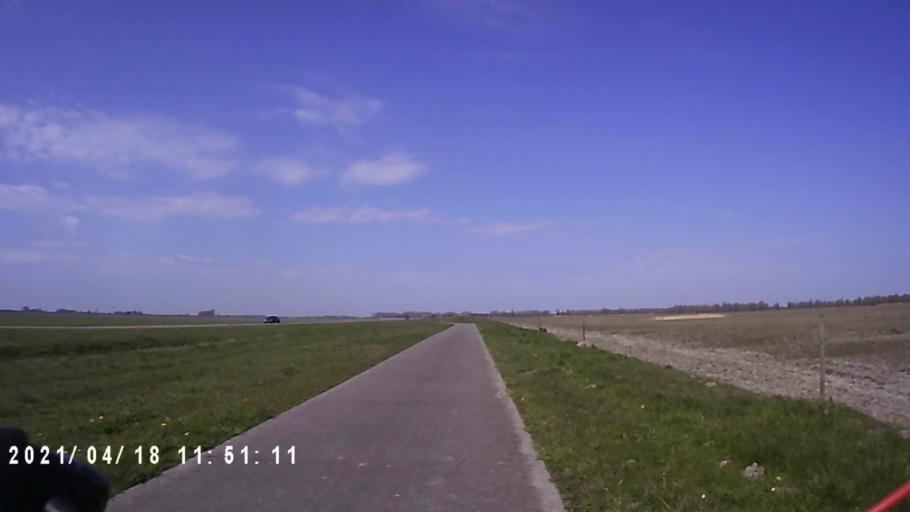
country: NL
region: Friesland
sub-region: Gemeente Kollumerland en Nieuwkruisland
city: Kollum
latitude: 53.3213
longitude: 6.2266
